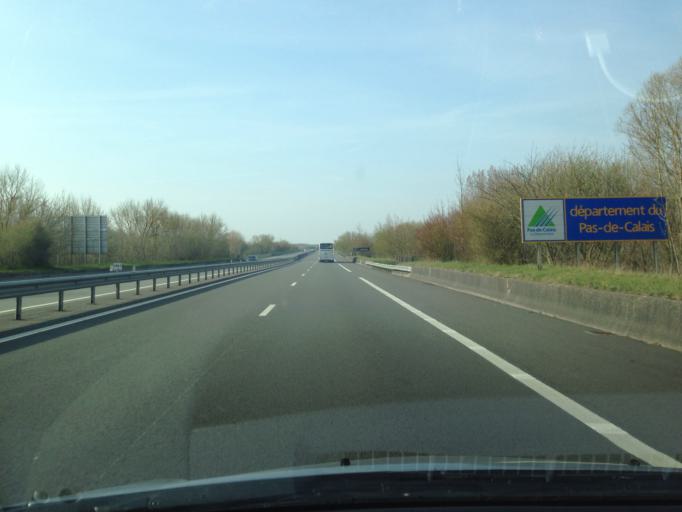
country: FR
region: Picardie
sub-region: Departement de la Somme
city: Quend
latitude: 50.3416
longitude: 1.6947
